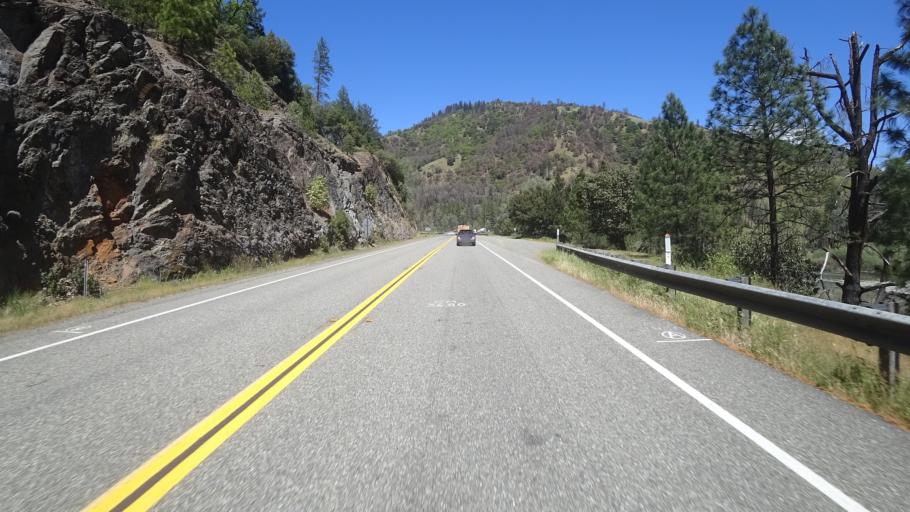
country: US
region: California
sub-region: Trinity County
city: Weaverville
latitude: 40.7686
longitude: -123.1291
